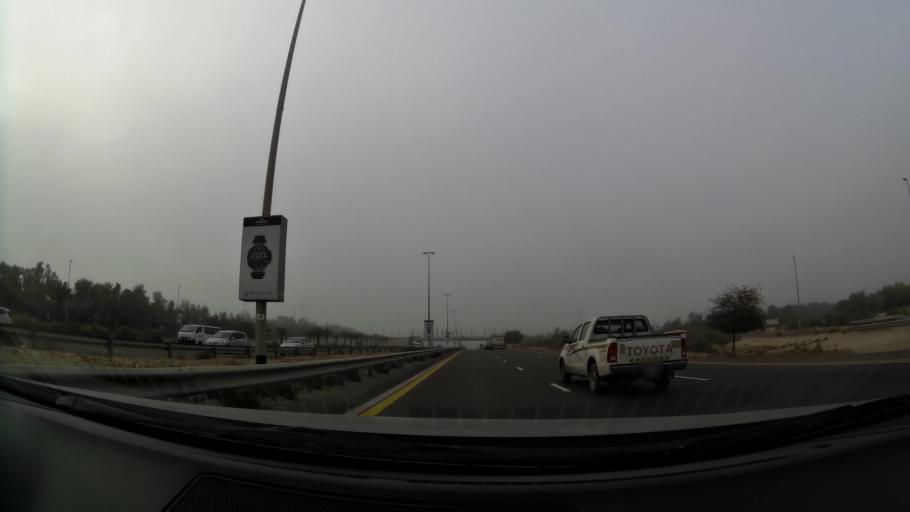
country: AE
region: Dubai
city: Dubai
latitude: 25.1531
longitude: 55.3377
